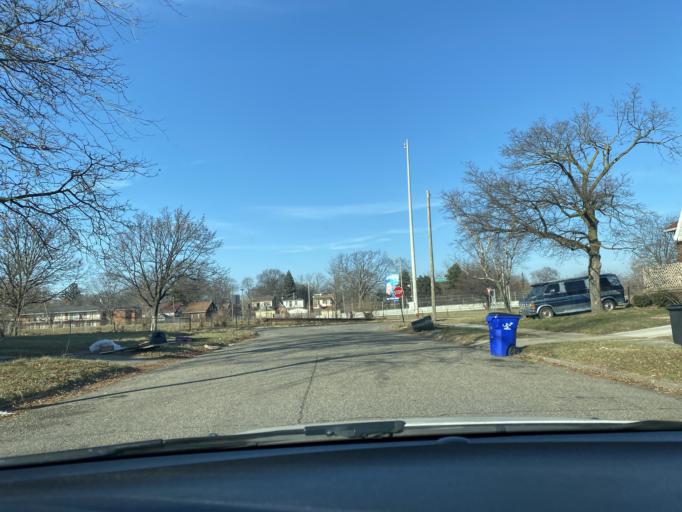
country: US
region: Michigan
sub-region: Wayne County
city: Grosse Pointe Park
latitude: 42.4079
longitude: -82.9484
